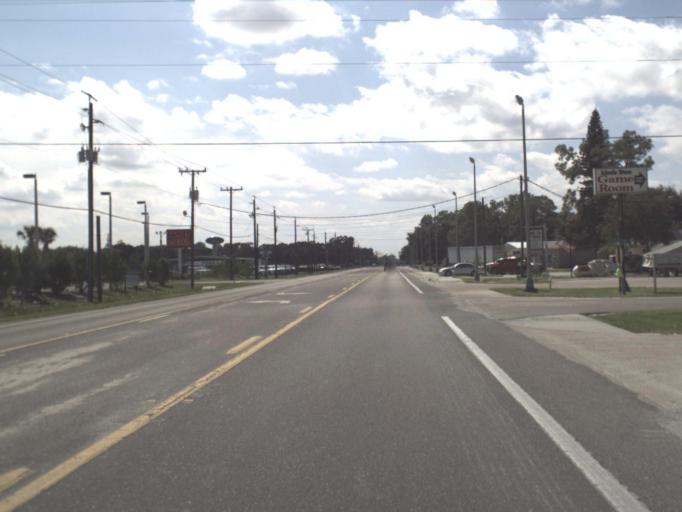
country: US
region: Florida
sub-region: Hendry County
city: LaBelle
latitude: 26.7513
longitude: -81.4381
